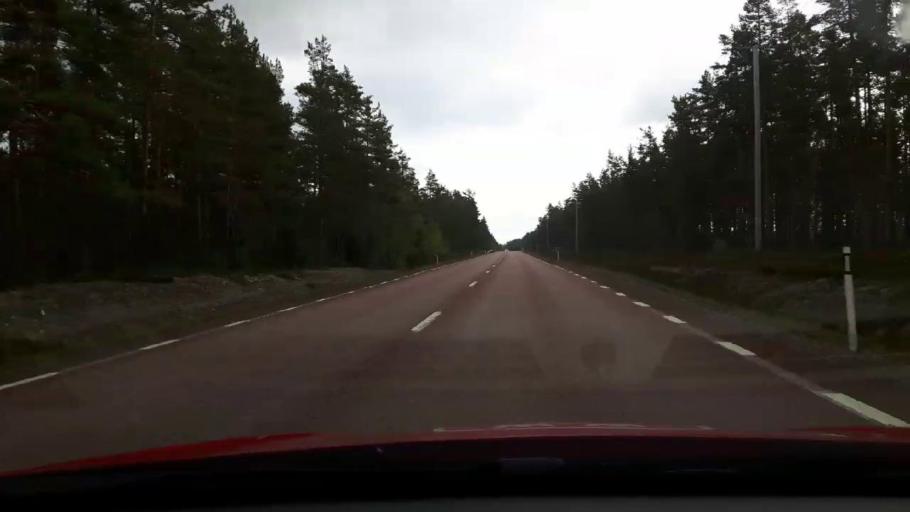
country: SE
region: Gaevleborg
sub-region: Soderhamns Kommun
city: Ljusne
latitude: 61.1077
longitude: 16.9392
